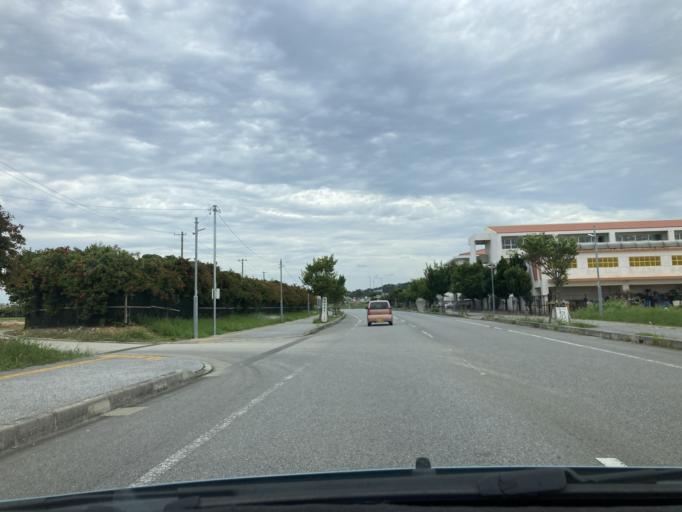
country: JP
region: Okinawa
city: Okinawa
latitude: 26.3948
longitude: 127.7410
